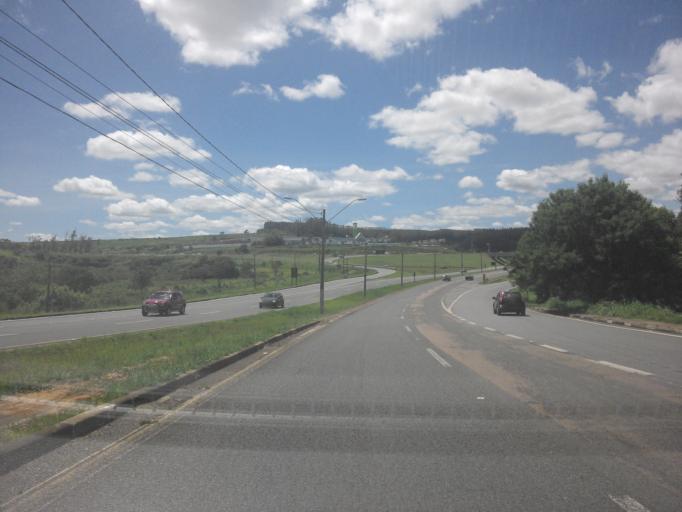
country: BR
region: Sao Paulo
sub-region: Campinas
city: Campinas
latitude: -22.8881
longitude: -47.0163
